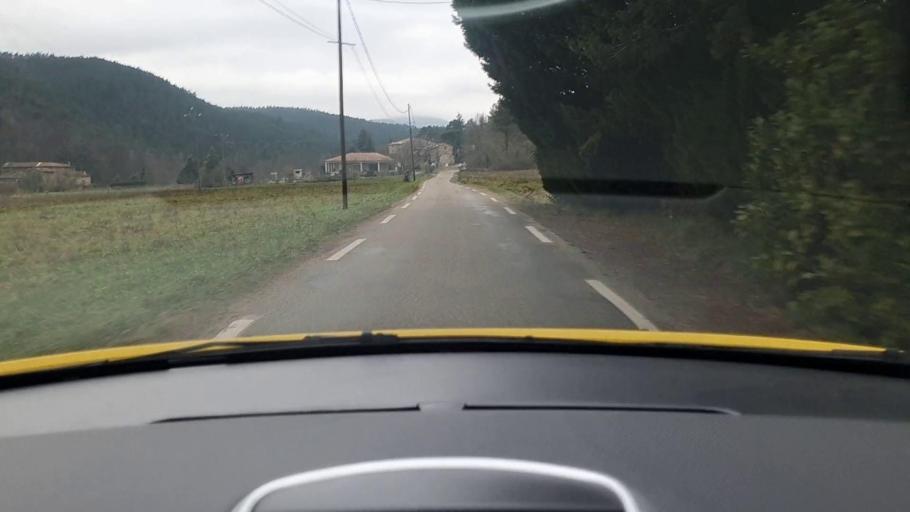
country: FR
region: Languedoc-Roussillon
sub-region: Departement du Gard
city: Besseges
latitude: 44.3205
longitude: 4.1265
